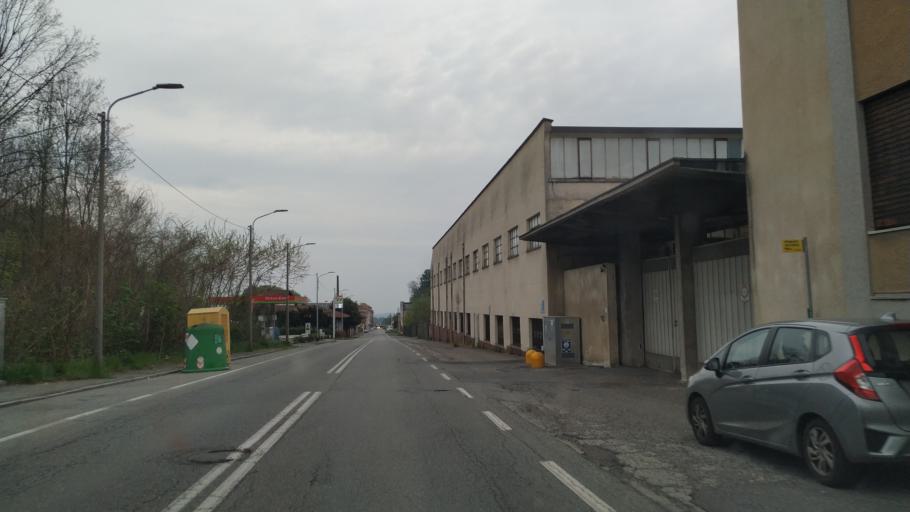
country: IT
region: Piedmont
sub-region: Provincia di Biella
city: Occhieppo Inferiore
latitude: 45.5622
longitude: 8.0240
